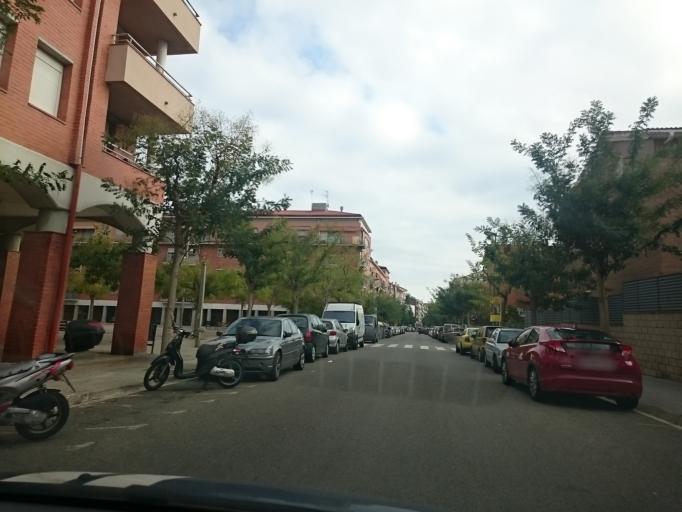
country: ES
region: Catalonia
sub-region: Provincia de Barcelona
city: Vilanova i la Geltru
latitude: 41.2235
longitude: 1.7134
